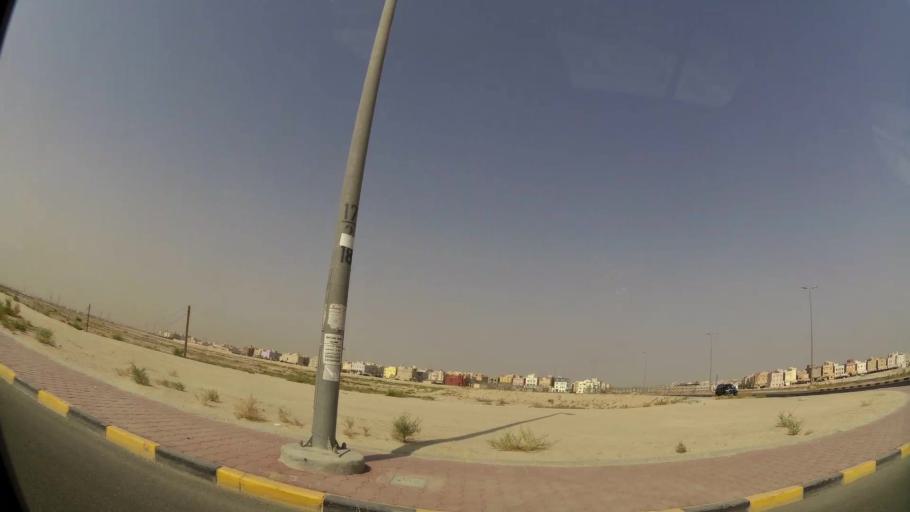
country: KW
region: Muhafazat al Jahra'
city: Al Jahra'
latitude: 29.3332
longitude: 47.7740
